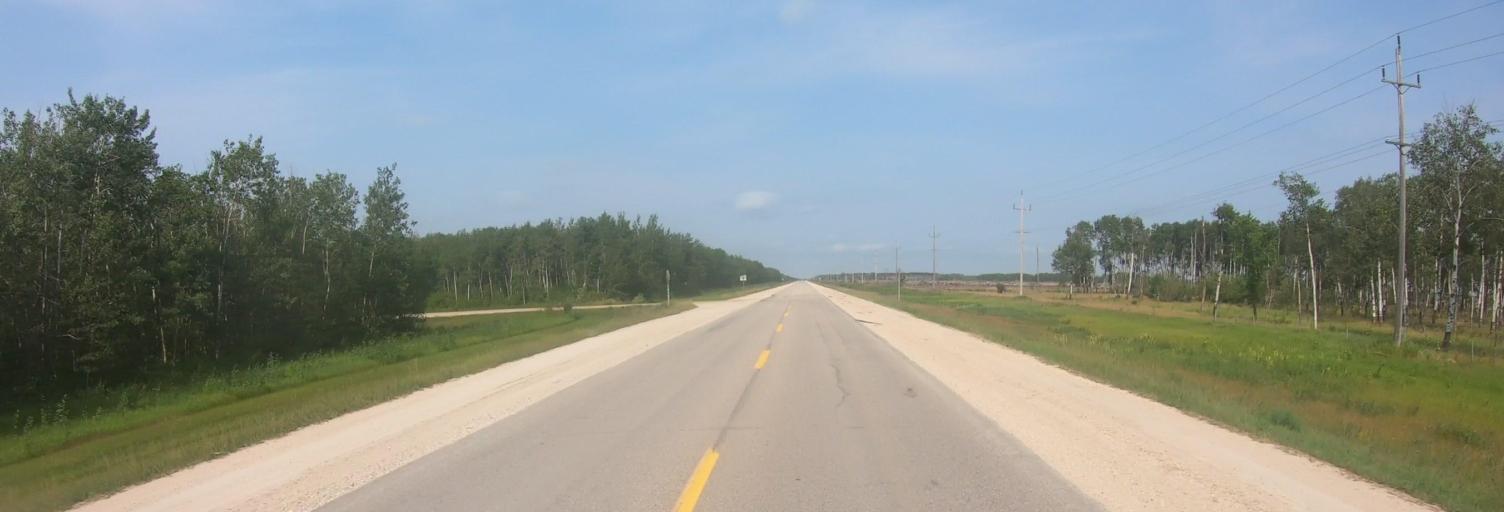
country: CA
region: Manitoba
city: La Broquerie
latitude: 49.3270
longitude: -96.6010
